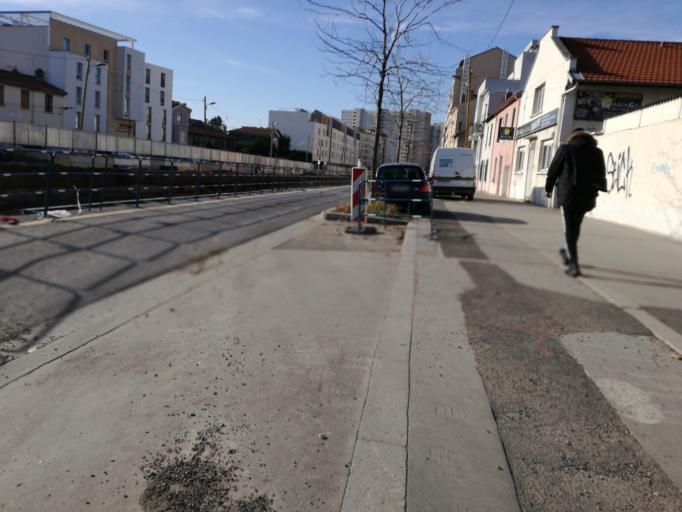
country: FR
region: Rhone-Alpes
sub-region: Departement du Rhone
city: Lyon
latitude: 45.7305
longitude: 4.8565
